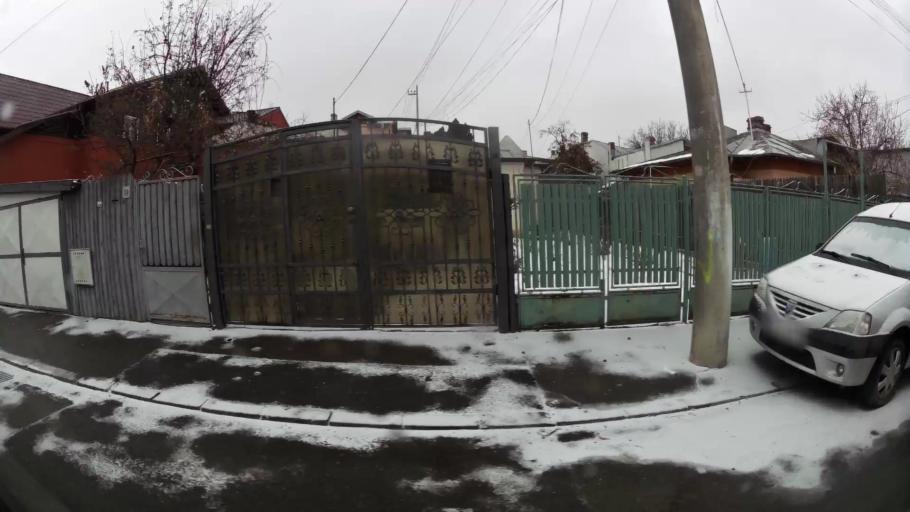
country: RO
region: Prahova
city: Ploiesti
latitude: 44.9490
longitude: 26.0156
